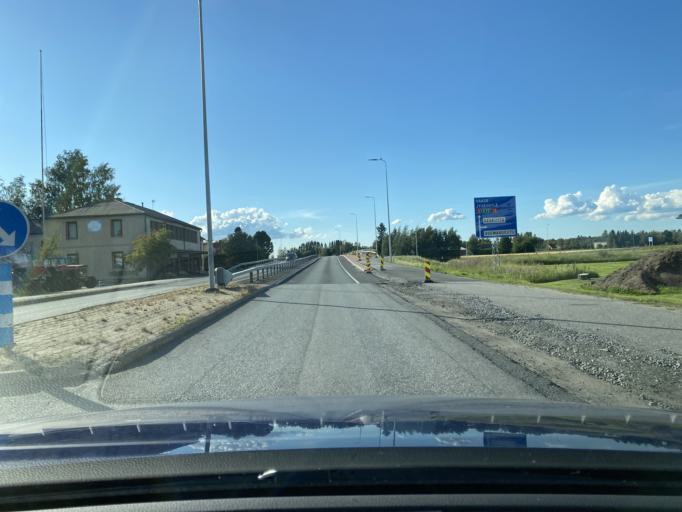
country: FI
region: Ostrobothnia
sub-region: Kyroenmaa
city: Laihia
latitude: 62.9814
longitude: 22.0066
